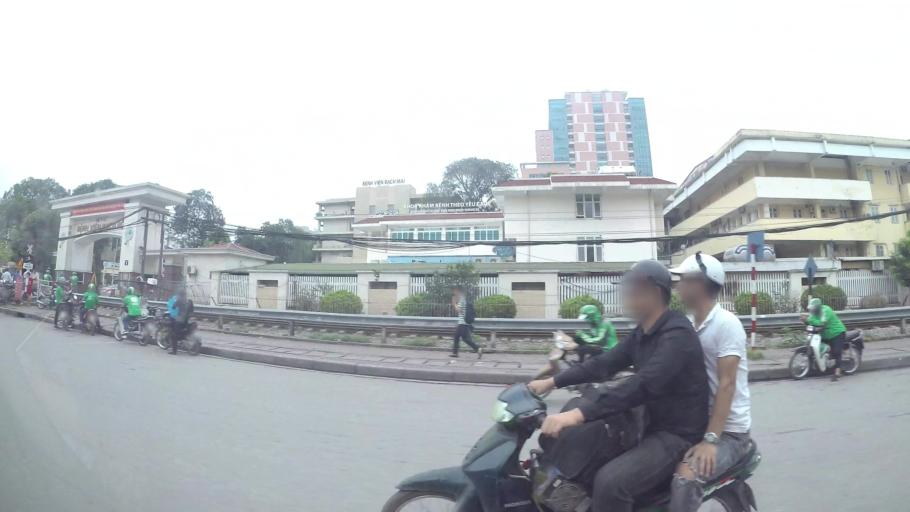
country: VN
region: Ha Noi
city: Hai BaTrung
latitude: 21.0023
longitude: 105.8412
